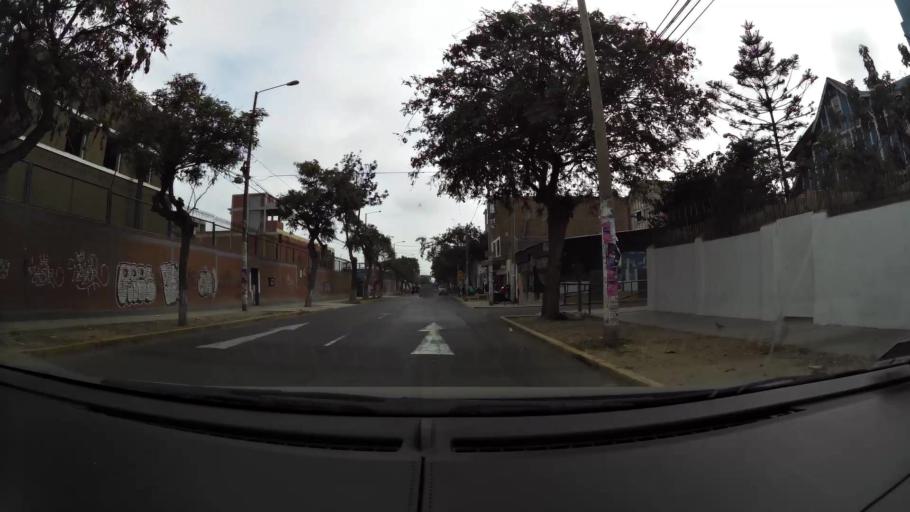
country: PE
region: La Libertad
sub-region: Provincia de Trujillo
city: Trujillo
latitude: -8.1009
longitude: -79.0203
